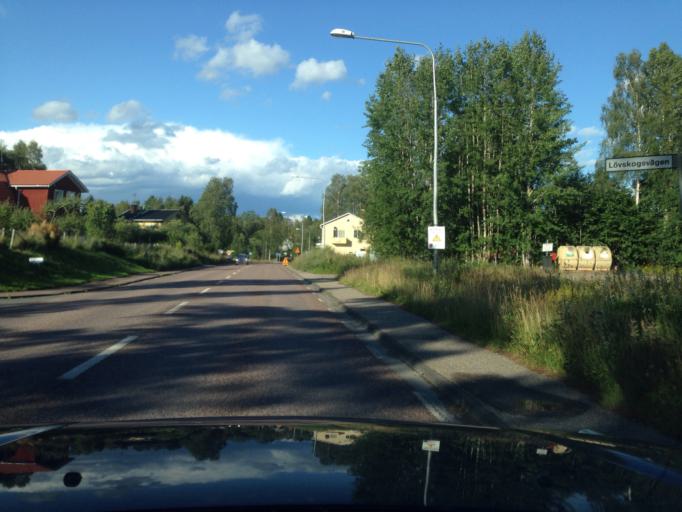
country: SE
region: Dalarna
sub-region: Ludvika Kommun
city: Ludvika
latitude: 60.1456
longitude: 15.0920
